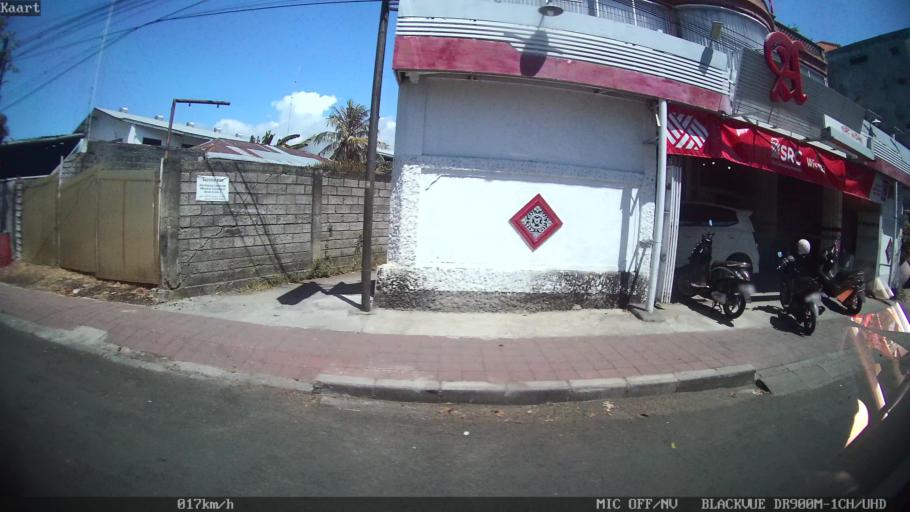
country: ID
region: Bali
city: Banjar Tambaksari
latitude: -8.1008
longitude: 115.0988
